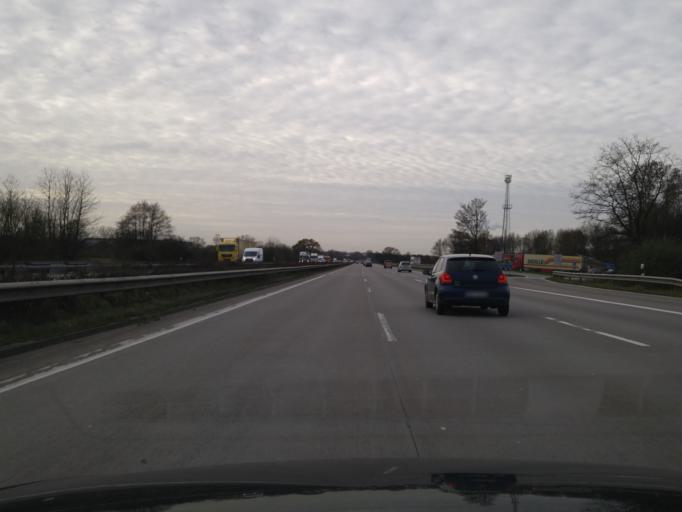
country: DE
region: Schleswig-Holstein
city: Braak
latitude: 53.6306
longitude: 10.2506
